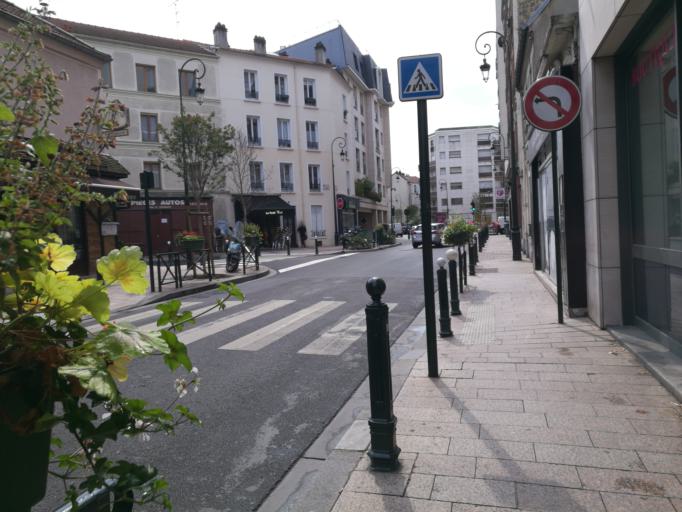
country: FR
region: Ile-de-France
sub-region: Departement des Hauts-de-Seine
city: Puteaux
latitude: 48.8855
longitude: 2.2427
